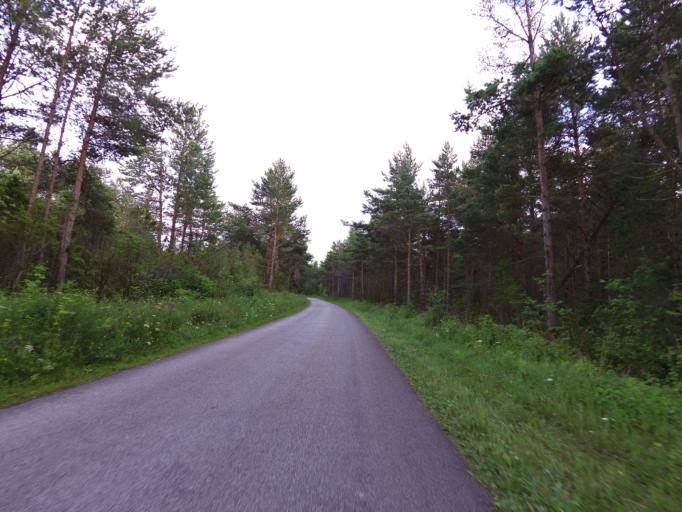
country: EE
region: Laeaene
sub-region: Vormsi vald
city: Hullo
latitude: 58.9819
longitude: 23.2497
